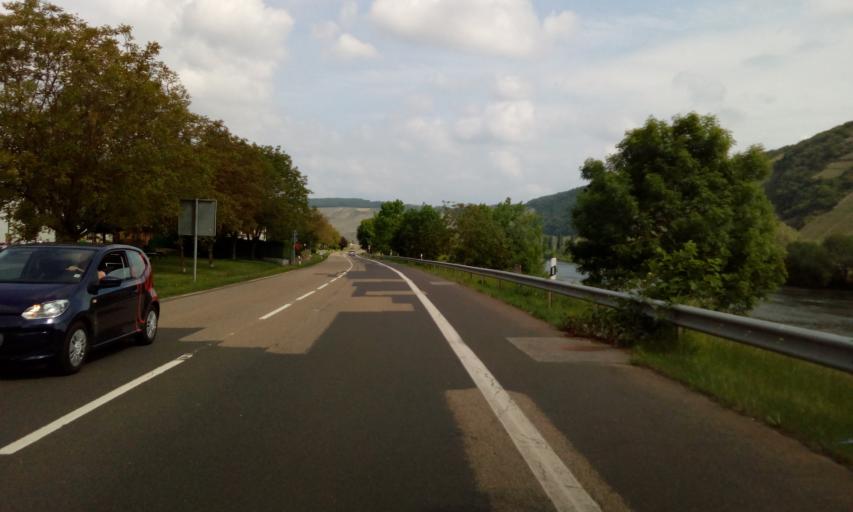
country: DE
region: Rheinland-Pfalz
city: Leiwen
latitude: 49.8219
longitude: 6.8838
